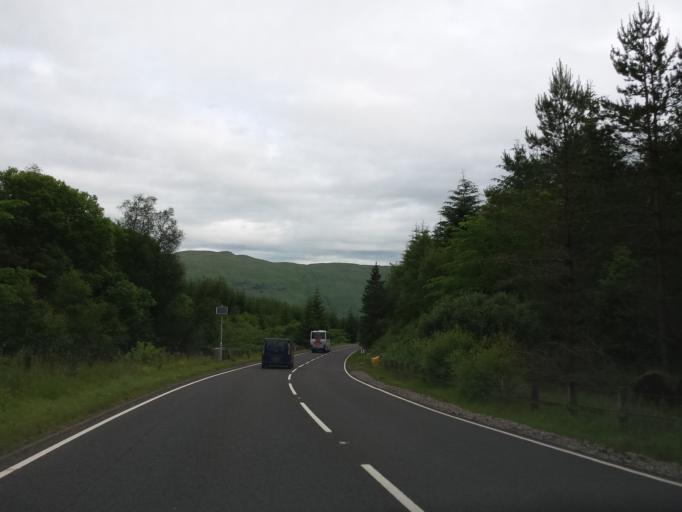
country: GB
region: Scotland
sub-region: Stirling
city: Callander
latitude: 56.4264
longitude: -4.3397
